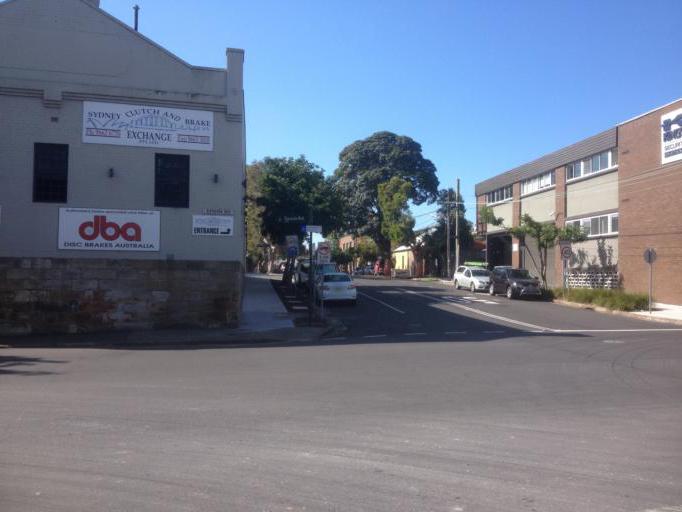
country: AU
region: New South Wales
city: Alexandria
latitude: -33.9103
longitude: 151.2036
